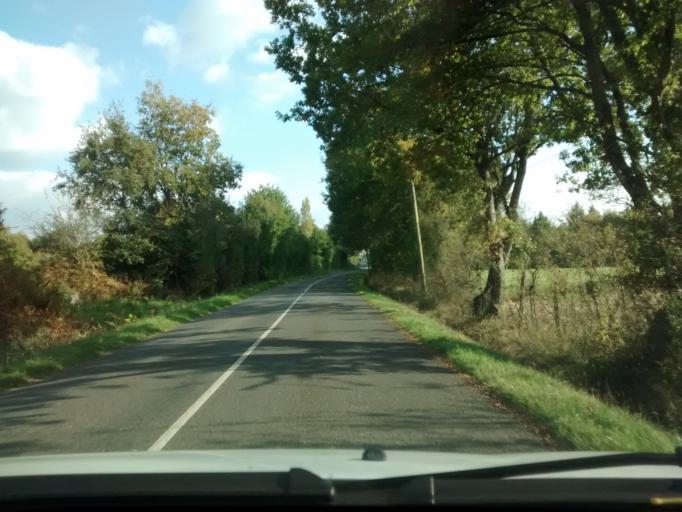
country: FR
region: Pays de la Loire
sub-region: Departement de la Loire-Atlantique
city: Orvault
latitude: 47.2804
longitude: -1.6423
